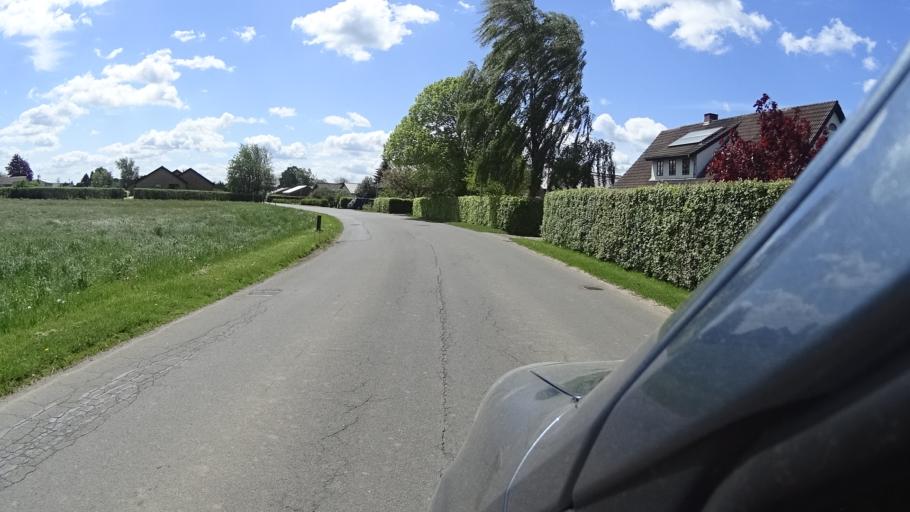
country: DK
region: South Denmark
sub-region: Fredericia Kommune
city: Taulov
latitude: 55.6110
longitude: 9.5630
